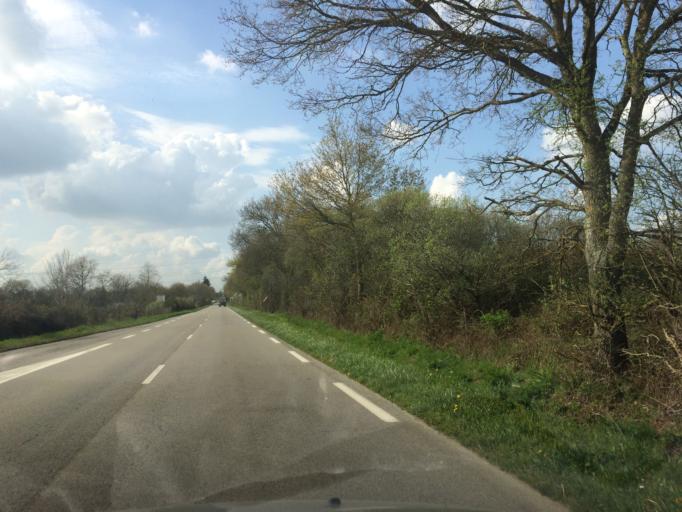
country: FR
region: Pays de la Loire
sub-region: Departement de la Loire-Atlantique
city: Heric
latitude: 47.4603
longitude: -1.6952
